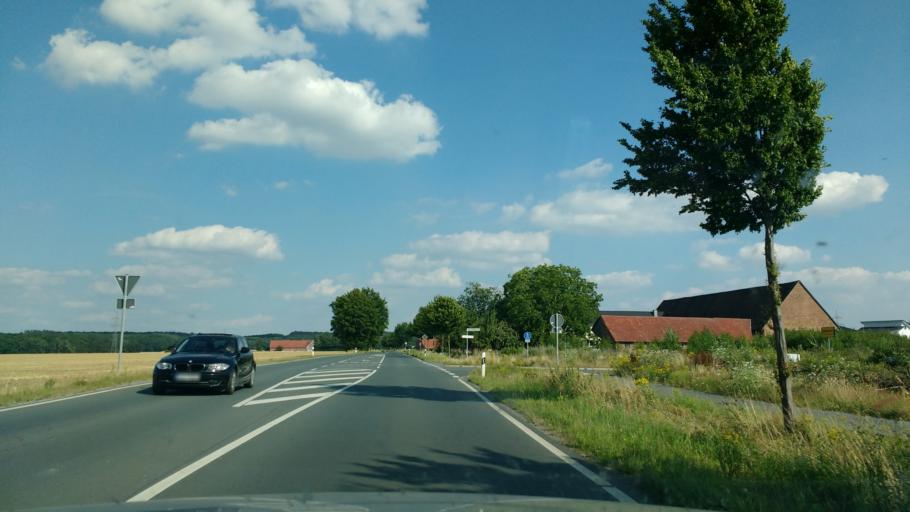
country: DE
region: North Rhine-Westphalia
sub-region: Regierungsbezirk Detmold
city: Salzkotten
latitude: 51.6692
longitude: 8.6263
